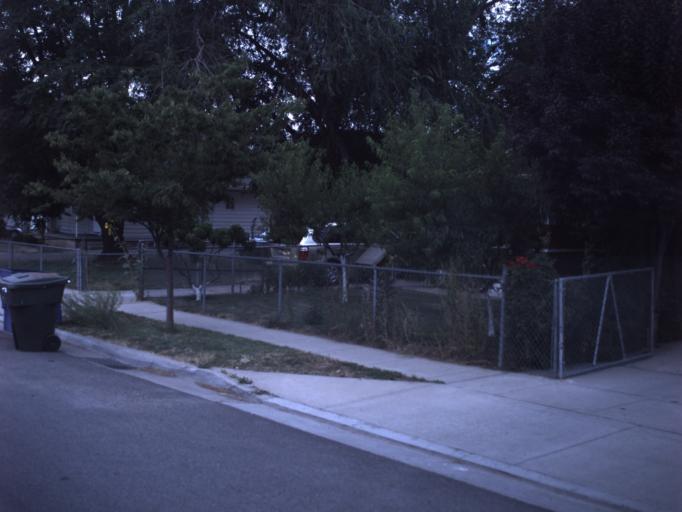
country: US
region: Utah
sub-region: Weber County
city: Ogden
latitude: 41.2101
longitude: -111.9630
